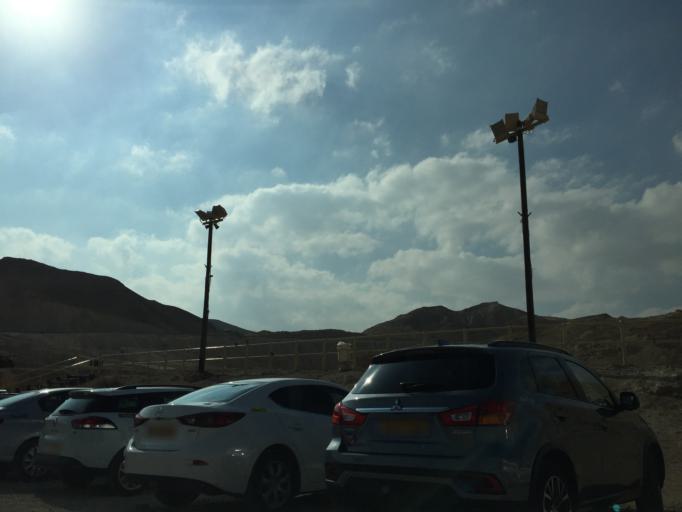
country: IL
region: Southern District
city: `En Boqeq
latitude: 31.3186
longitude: 35.3478
